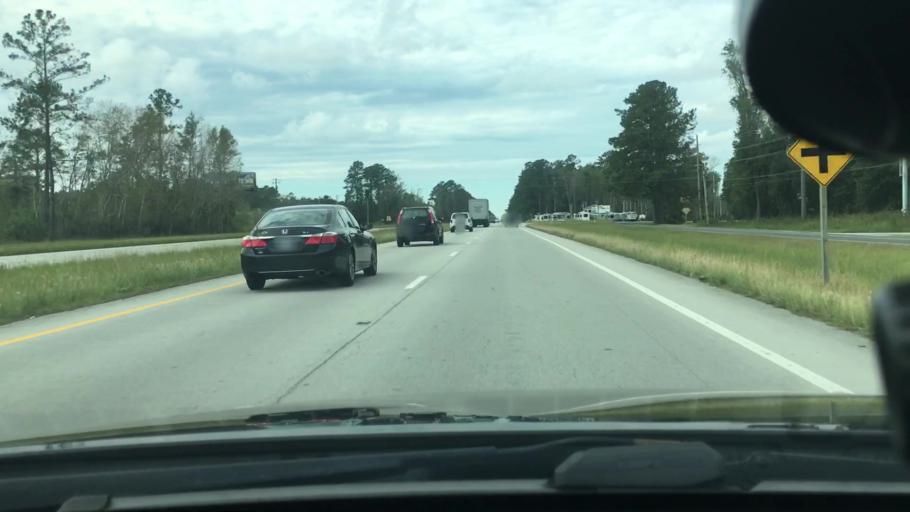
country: US
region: North Carolina
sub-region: Craven County
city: Neuse Forest
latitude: 35.0117
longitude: -76.9928
